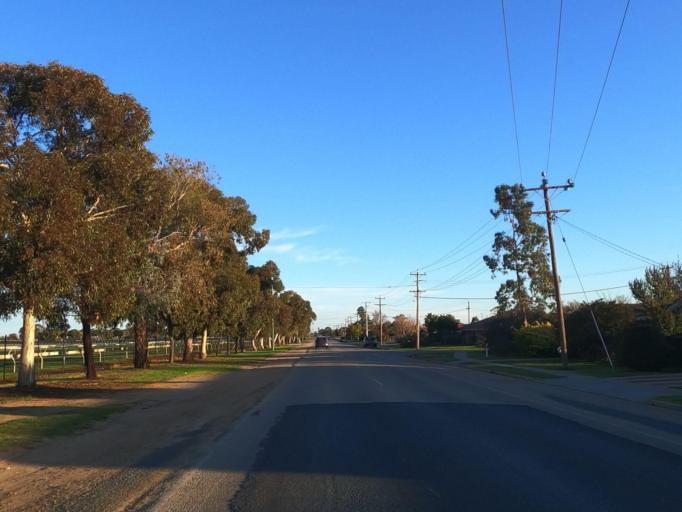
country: AU
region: Victoria
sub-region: Swan Hill
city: Swan Hill
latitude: -35.3495
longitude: 143.5547
